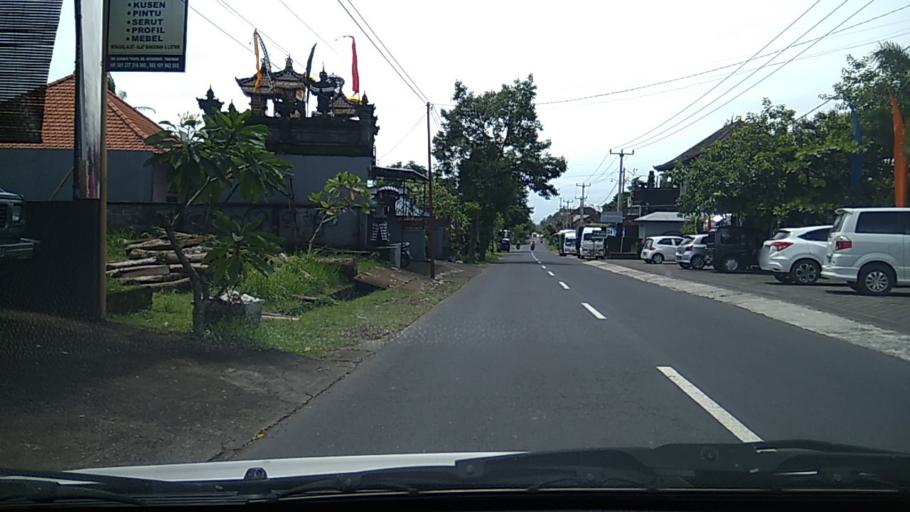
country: ID
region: Bali
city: Wanasari Baleran
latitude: -8.4708
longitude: 115.1371
